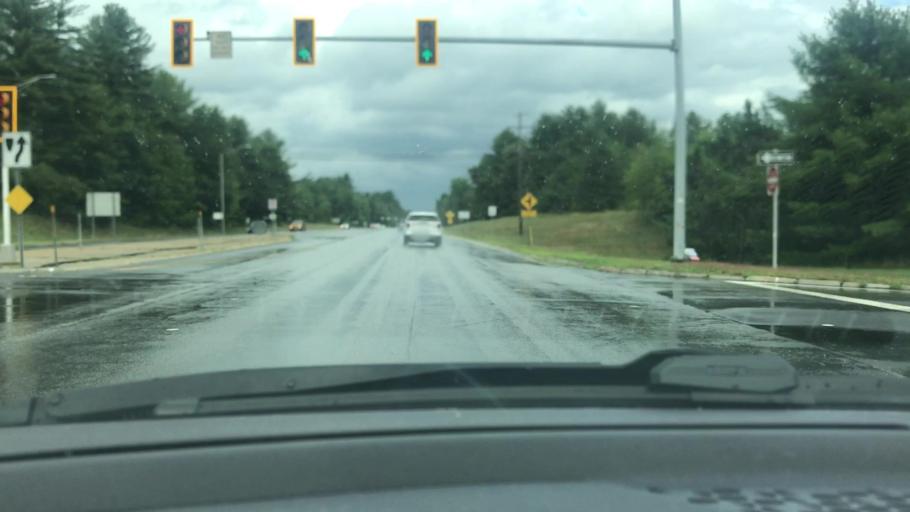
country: US
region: New Hampshire
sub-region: Merrimack County
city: East Concord
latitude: 43.2356
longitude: -71.4698
